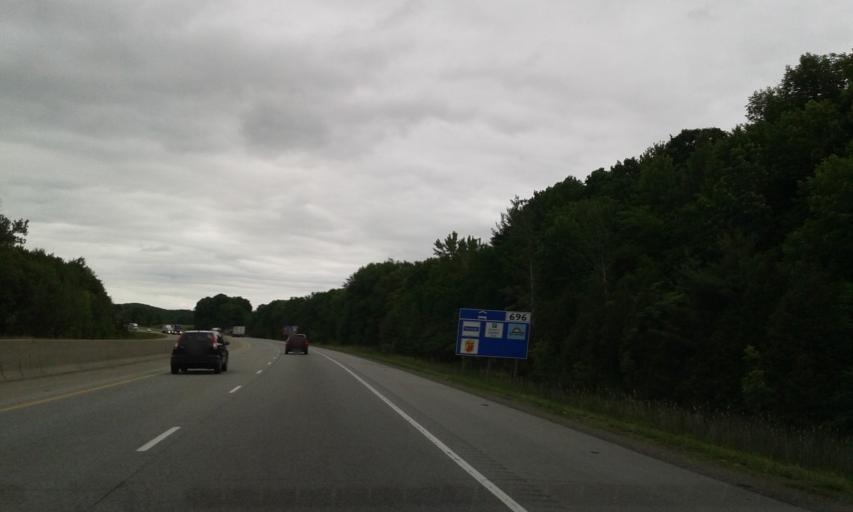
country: CA
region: Ontario
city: Brockville
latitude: 44.5657
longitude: -75.7422
